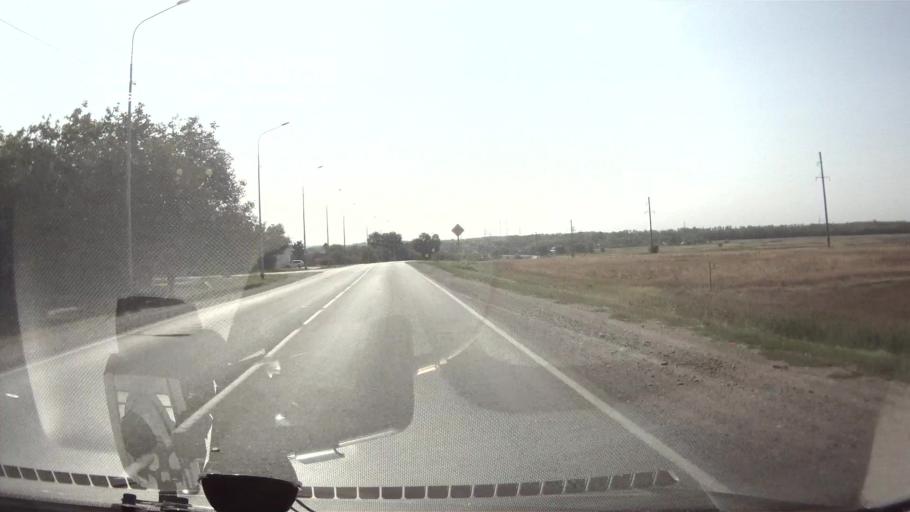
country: RU
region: Krasnodarskiy
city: Belaya Glina
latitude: 46.0870
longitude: 40.8314
